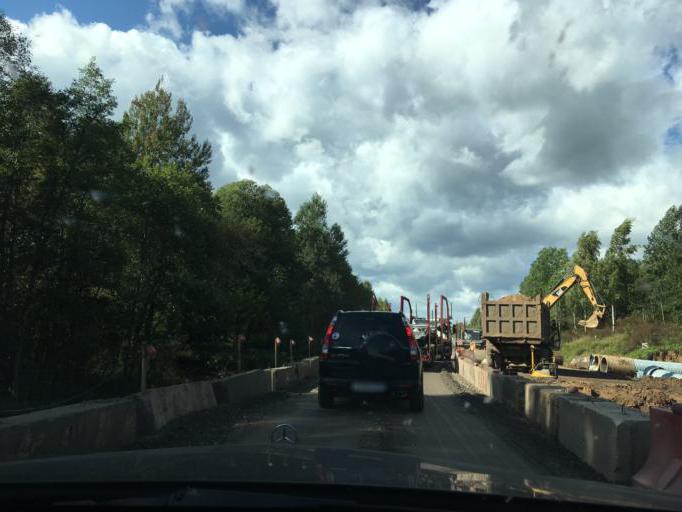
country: RU
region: Pskov
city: Novosokol'niki
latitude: 56.2813
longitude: 30.2978
